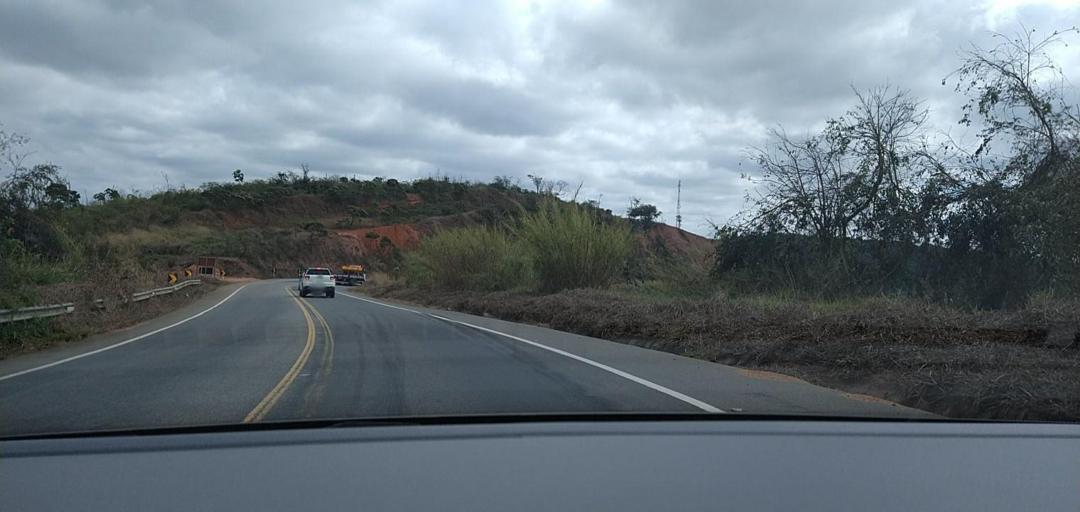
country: BR
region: Minas Gerais
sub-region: Ponte Nova
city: Ponte Nova
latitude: -20.5412
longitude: -42.8878
